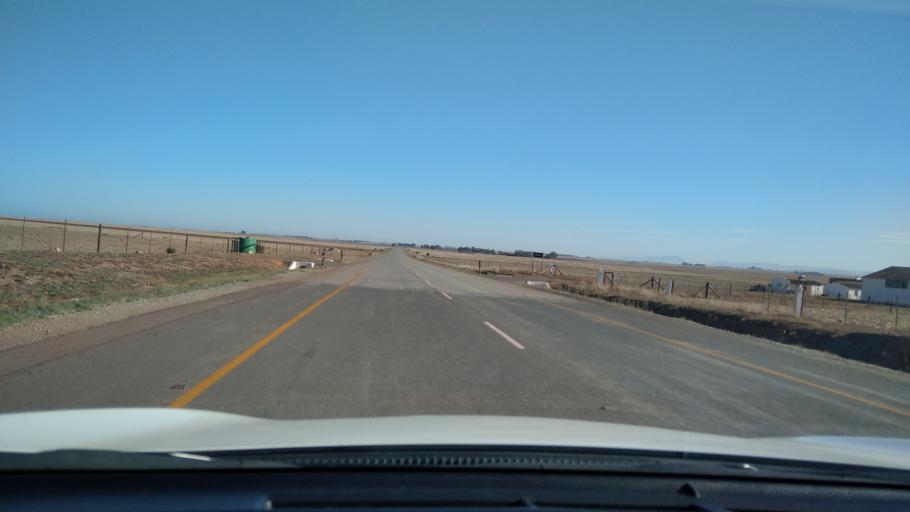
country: ZA
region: Western Cape
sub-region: West Coast District Municipality
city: Moorreesburg
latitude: -33.3043
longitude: 18.6161
